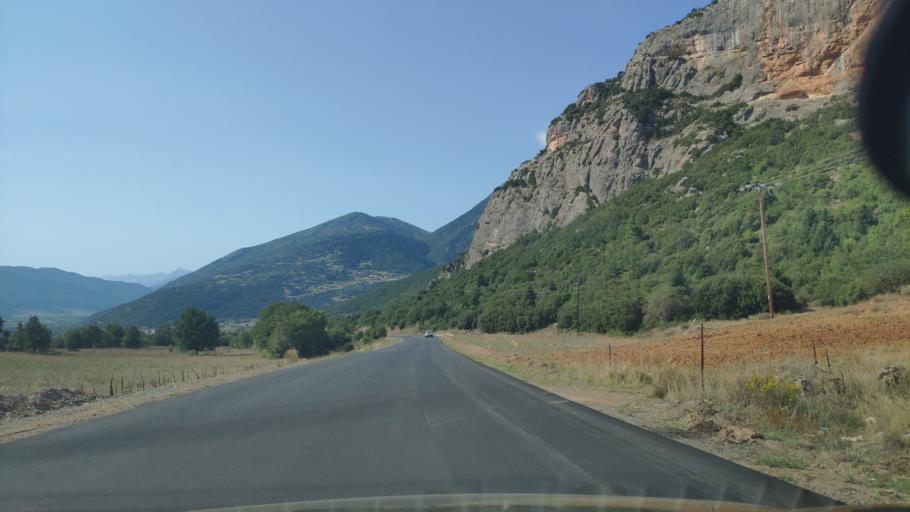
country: GR
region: Peloponnese
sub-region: Nomos Korinthias
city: Nemea
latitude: 37.9353
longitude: 22.5376
